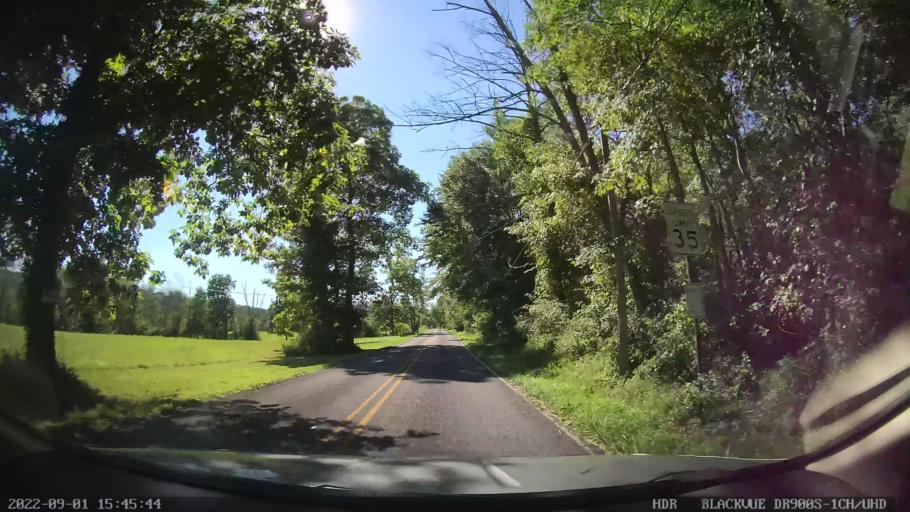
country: US
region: Pennsylvania
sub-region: Berks County
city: Topton
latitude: 40.4698
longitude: -75.7015
